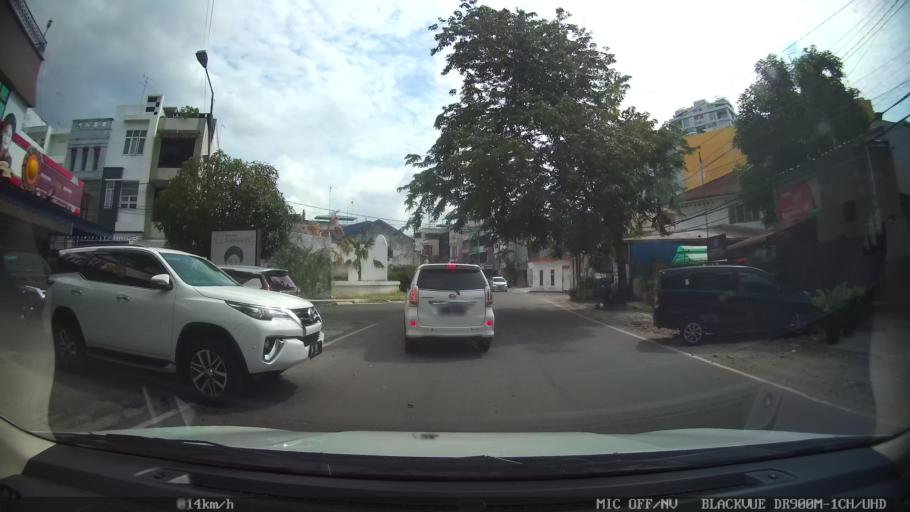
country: ID
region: North Sumatra
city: Medan
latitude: 3.5861
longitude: 98.6698
